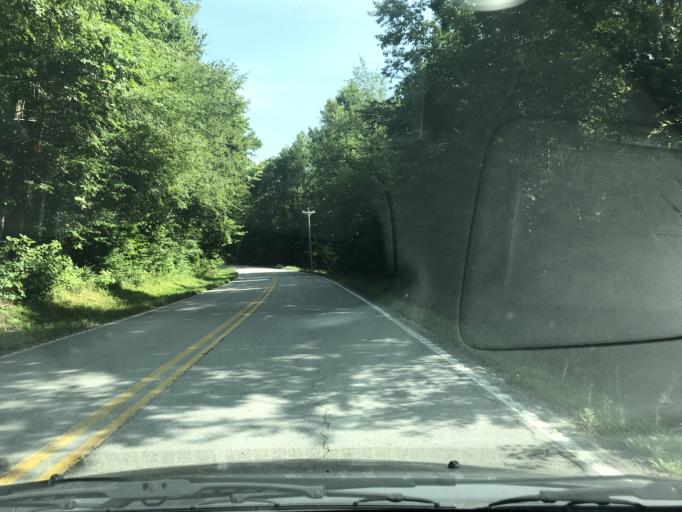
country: US
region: Tennessee
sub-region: Hamilton County
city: Lakesite
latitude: 35.2495
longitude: -85.0669
